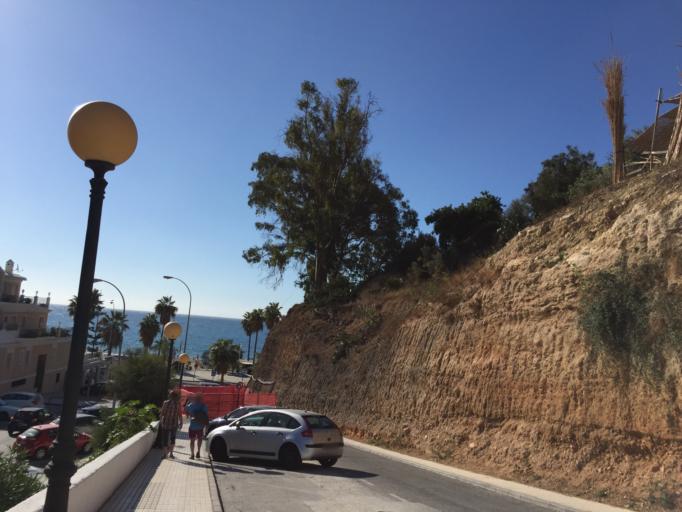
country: ES
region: Andalusia
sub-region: Provincia de Malaga
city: Nerja
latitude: 36.7506
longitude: -3.8697
